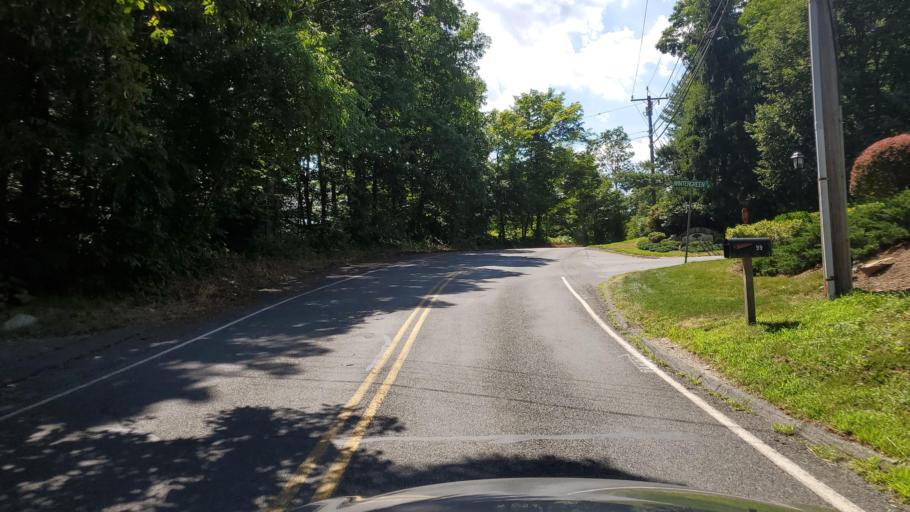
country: US
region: Connecticut
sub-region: Fairfield County
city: Newtown
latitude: 41.3227
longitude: -73.2741
